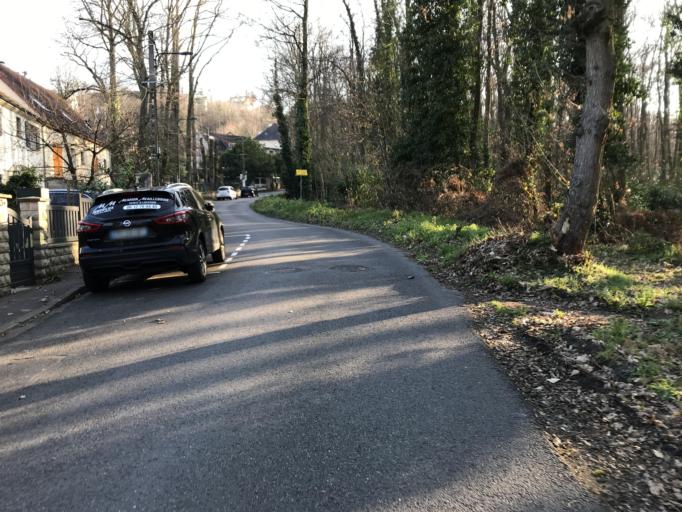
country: FR
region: Ile-de-France
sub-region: Departement de l'Essonne
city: Orsay
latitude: 48.6977
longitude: 2.2065
